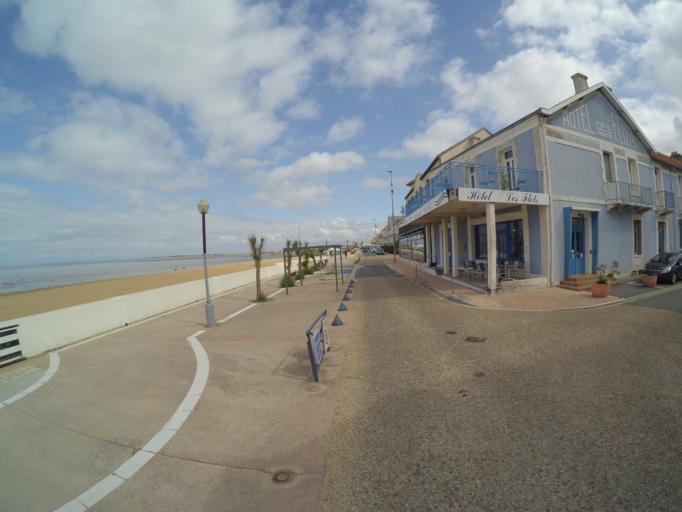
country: FR
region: Poitou-Charentes
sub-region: Departement de la Charente-Maritime
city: Chatelaillon-Plage
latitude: 46.0747
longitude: -1.0935
